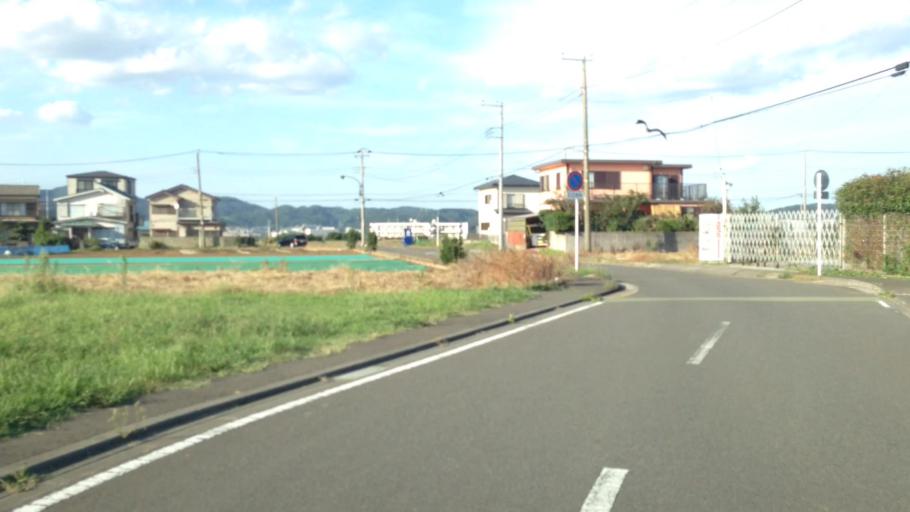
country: JP
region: Kanagawa
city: Miura
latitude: 35.2022
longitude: 139.6151
